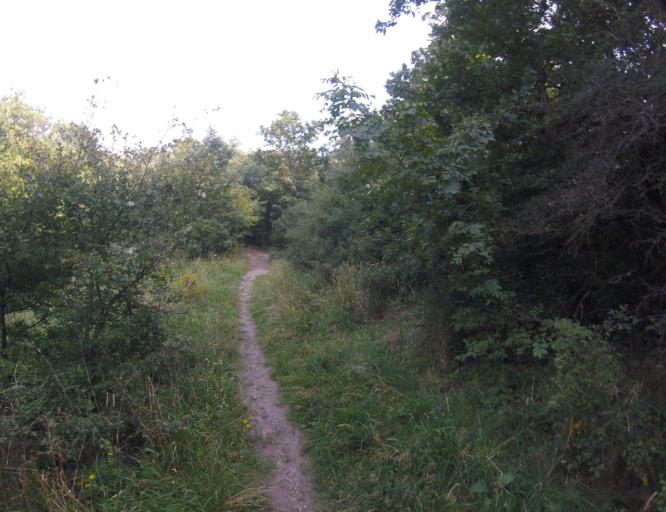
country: HU
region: Pest
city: Nagykovacsi
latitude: 47.6765
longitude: 19.0134
